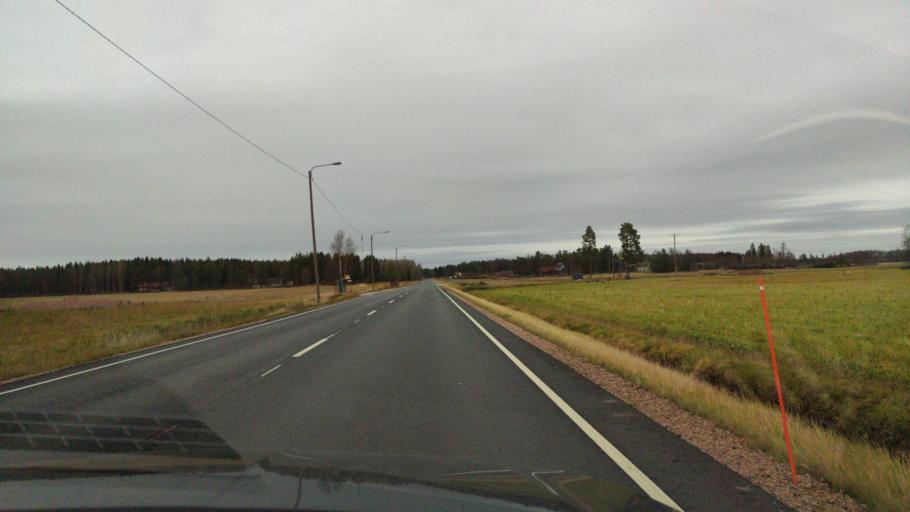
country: FI
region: Varsinais-Suomi
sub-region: Loimaa
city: Aura
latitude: 60.6724
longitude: 22.4367
